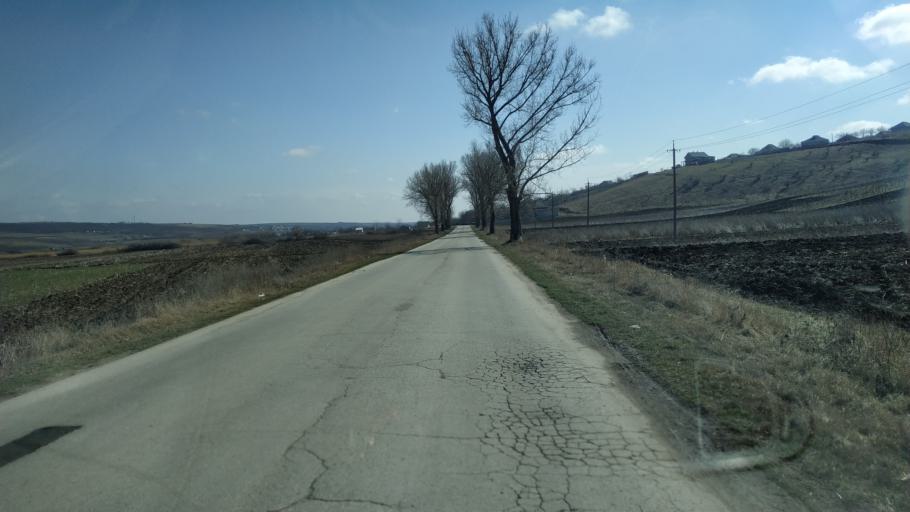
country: MD
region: Hincesti
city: Hincesti
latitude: 46.9403
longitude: 28.6293
